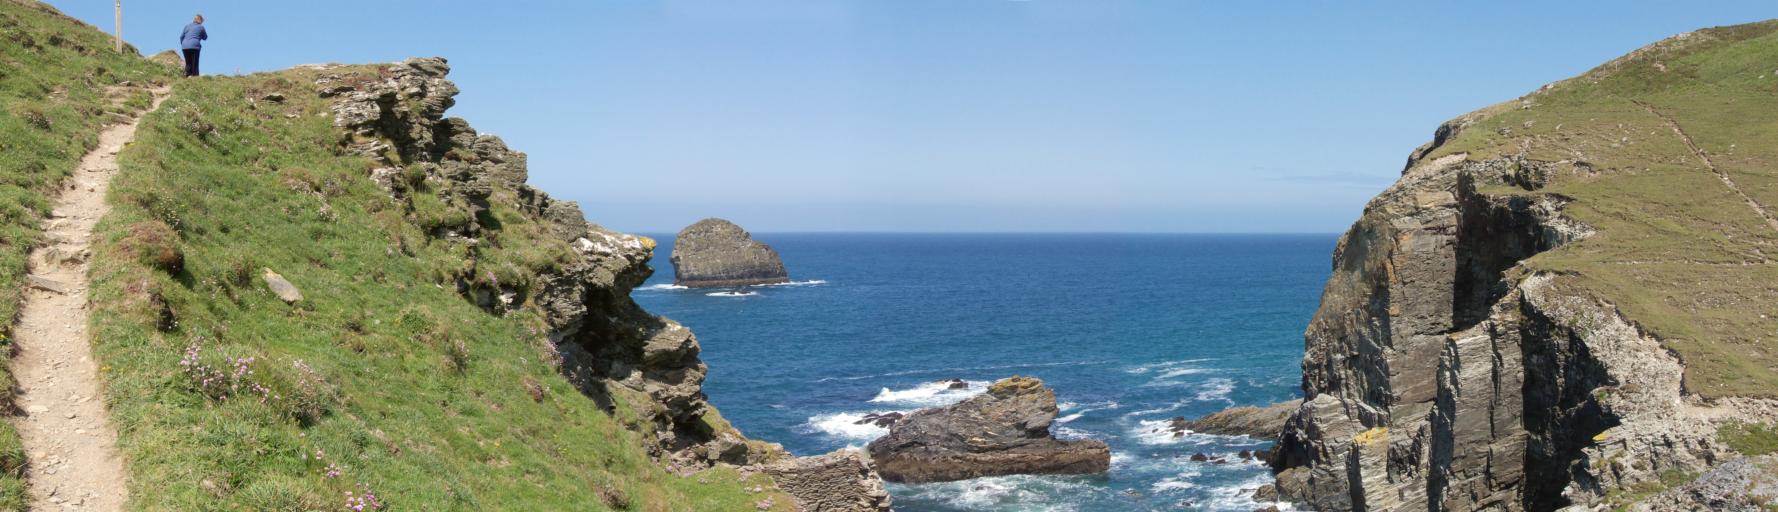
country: GB
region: England
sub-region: Cornwall
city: Tintagel
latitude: 50.6397
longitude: -4.7650
